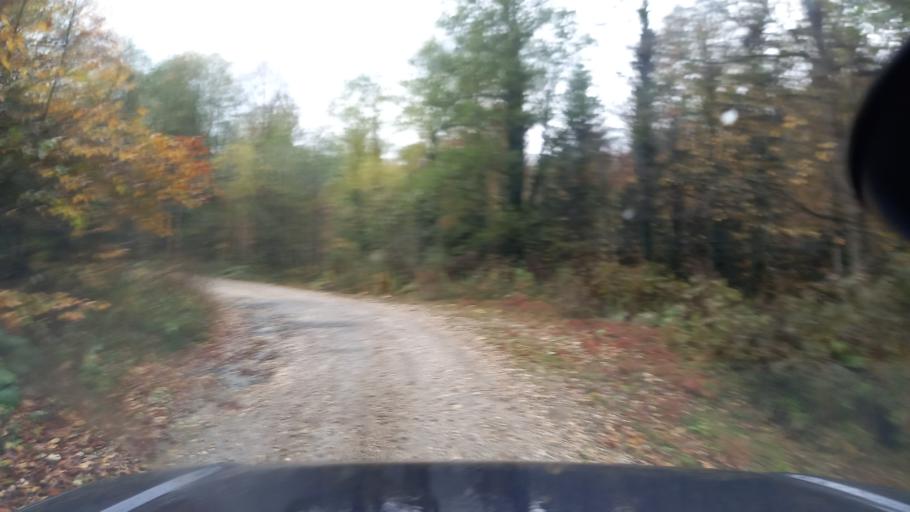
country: RU
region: Krasnodarskiy
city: Neftegorsk
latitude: 44.0312
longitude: 39.8369
